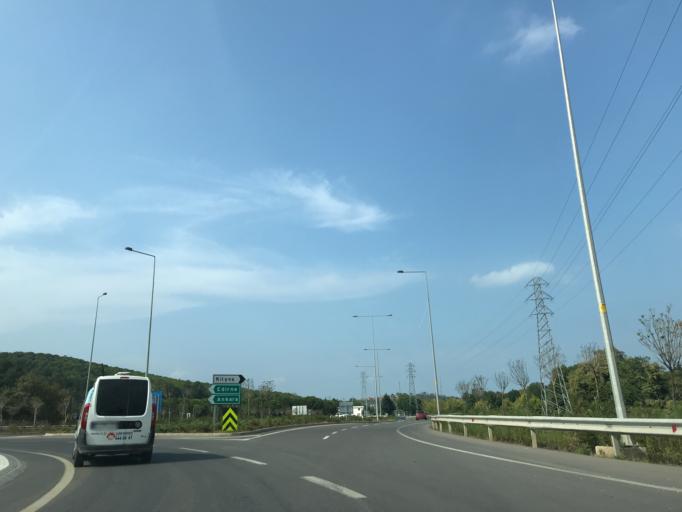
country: TR
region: Istanbul
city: Arikoey
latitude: 41.2366
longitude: 29.0418
